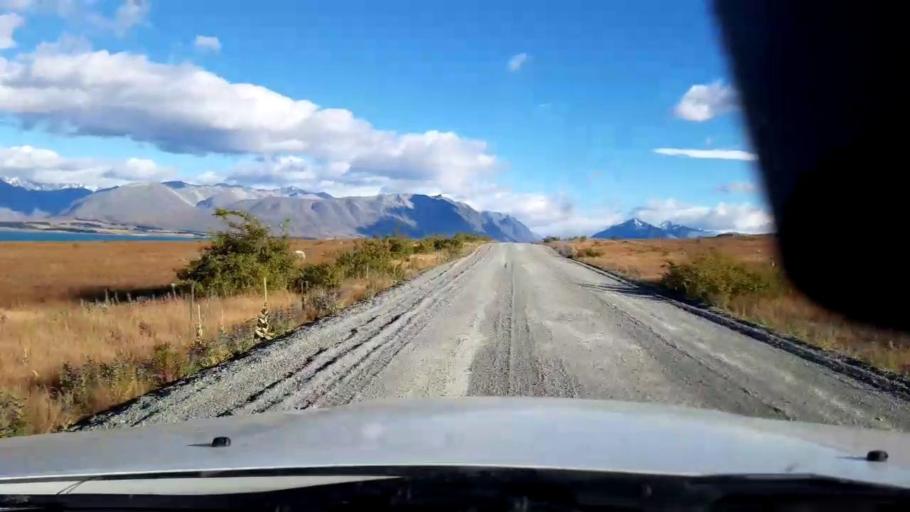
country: NZ
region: Canterbury
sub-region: Timaru District
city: Pleasant Point
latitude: -43.9191
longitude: 170.5592
